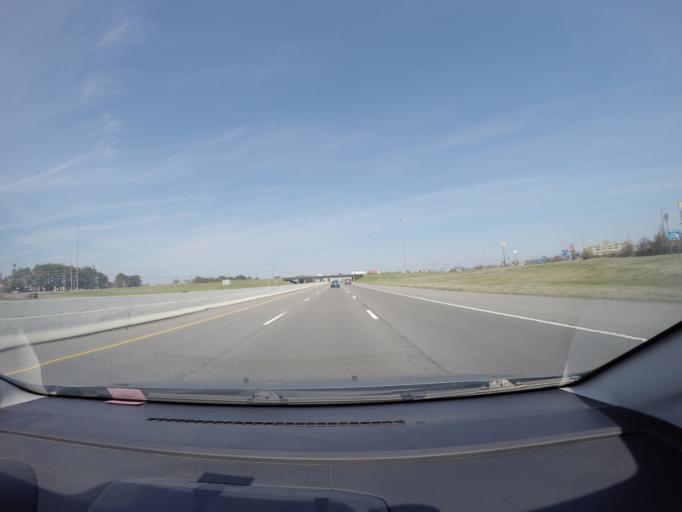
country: US
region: Tennessee
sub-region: Rutherford County
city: Murfreesboro
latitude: 35.8103
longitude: -86.3944
